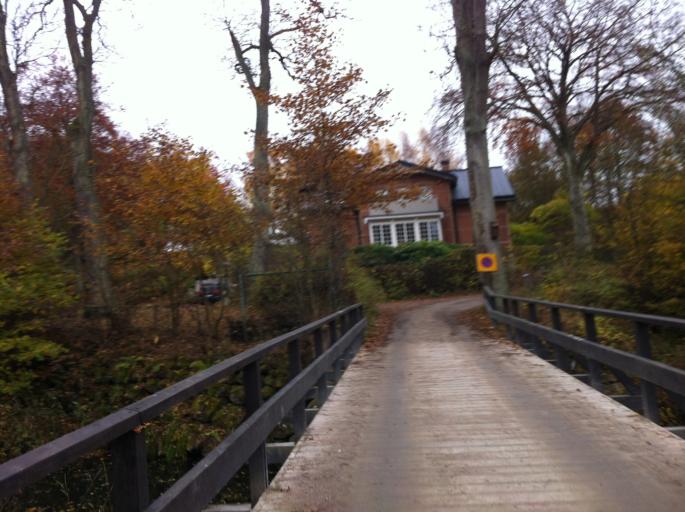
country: SE
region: Skane
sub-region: Helsingborg
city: Gantofta
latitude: 55.9991
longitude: 12.7865
